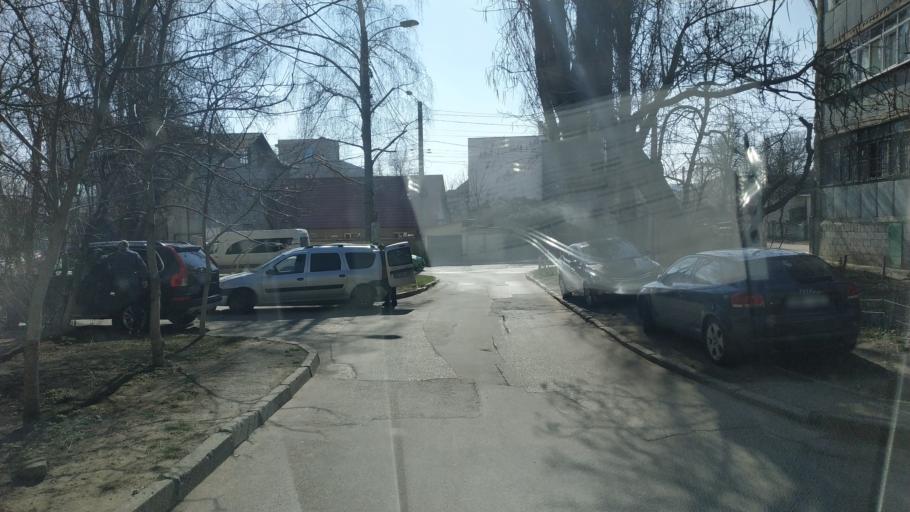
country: MD
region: Chisinau
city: Chisinau
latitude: 47.0286
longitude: 28.8015
